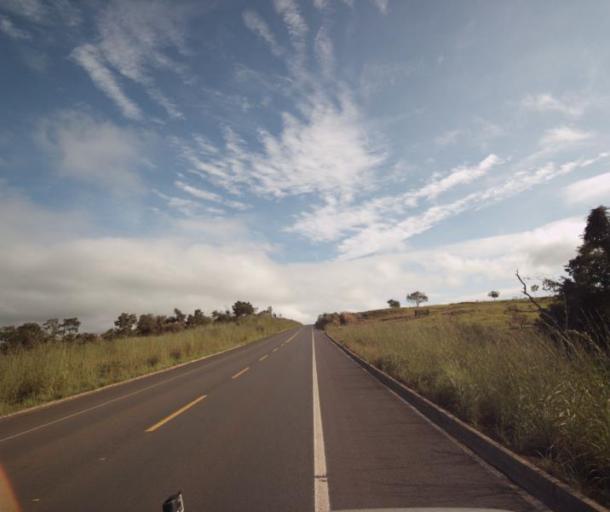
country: BR
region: Goias
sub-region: Padre Bernardo
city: Padre Bernardo
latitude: -15.4344
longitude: -48.6202
